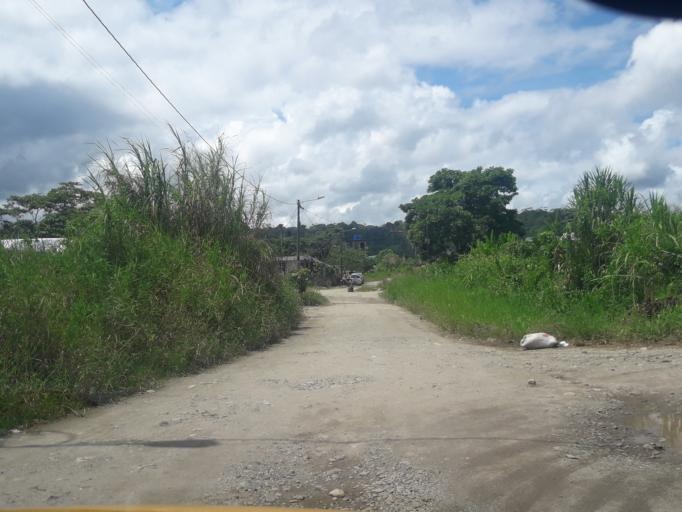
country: EC
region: Napo
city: Tena
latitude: -1.0071
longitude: -77.8181
